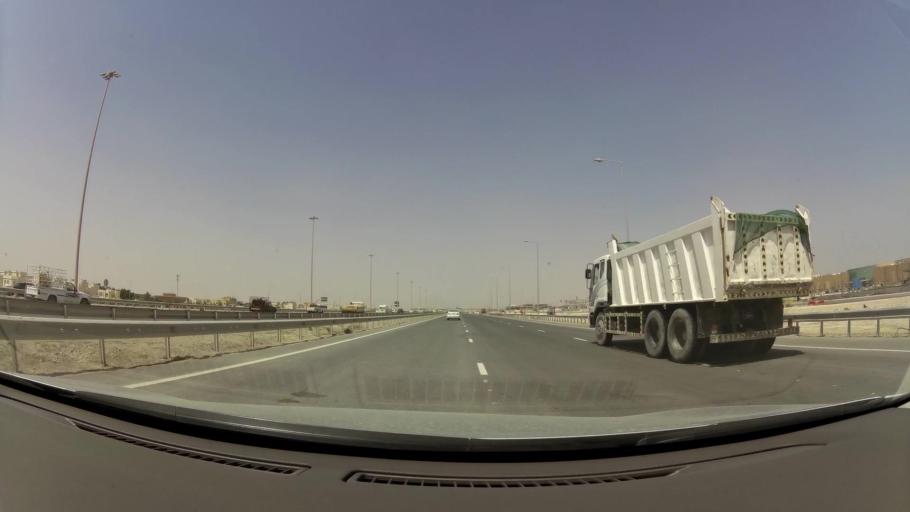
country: QA
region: Baladiyat Umm Salal
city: Umm Salal Muhammad
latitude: 25.3830
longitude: 51.4388
